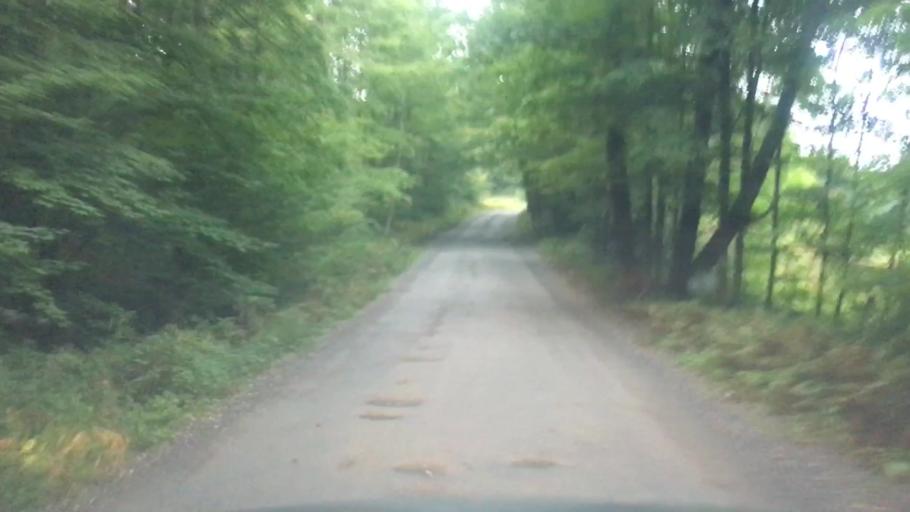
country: US
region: Vermont
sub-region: Windham County
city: Dover
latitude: 42.8495
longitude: -72.7747
